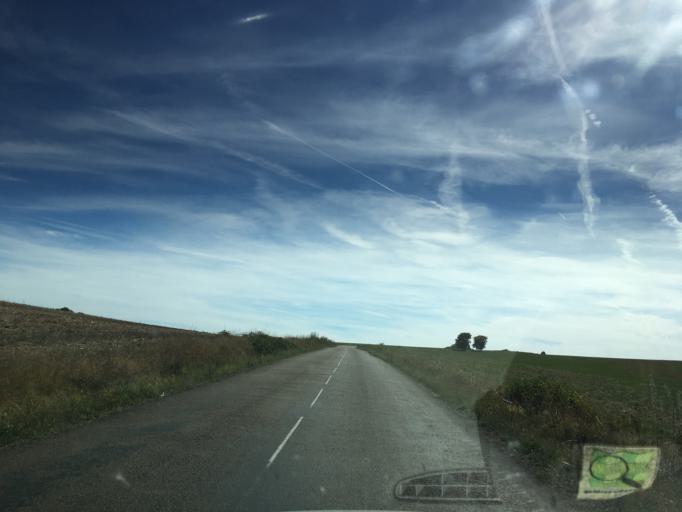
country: FR
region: Bourgogne
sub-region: Departement de l'Yonne
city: Vermenton
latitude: 47.5916
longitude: 3.6977
